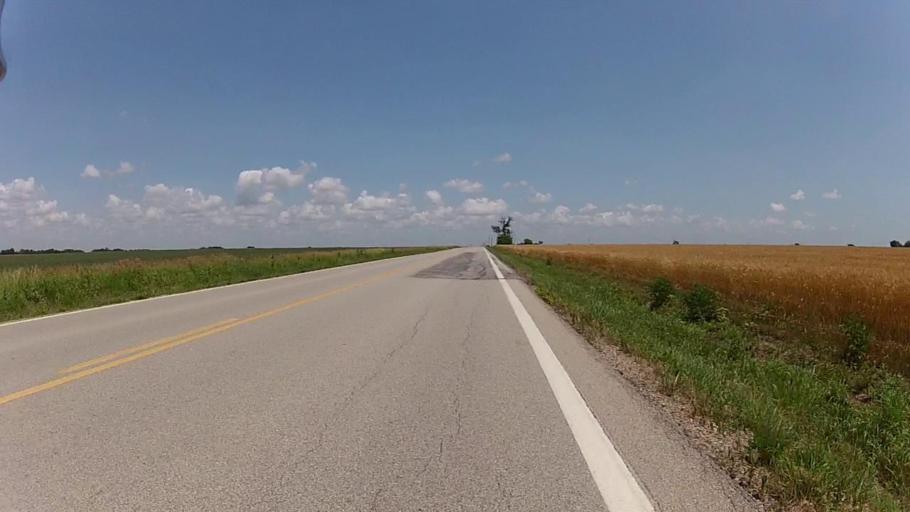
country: US
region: Kansas
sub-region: Labette County
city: Altamont
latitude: 37.1926
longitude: -95.4354
